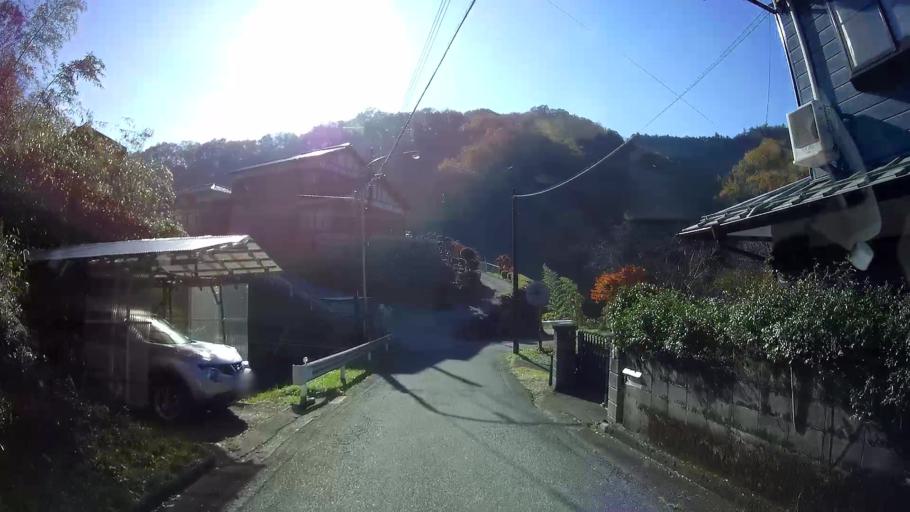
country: JP
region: Yamanashi
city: Uenohara
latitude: 35.5938
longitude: 139.1257
